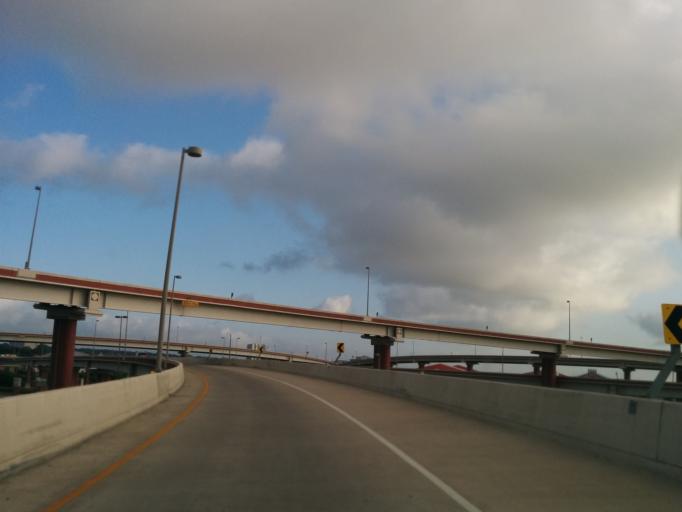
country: US
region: Texas
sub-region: Bexar County
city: Alamo Heights
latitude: 29.5185
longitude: -98.4786
